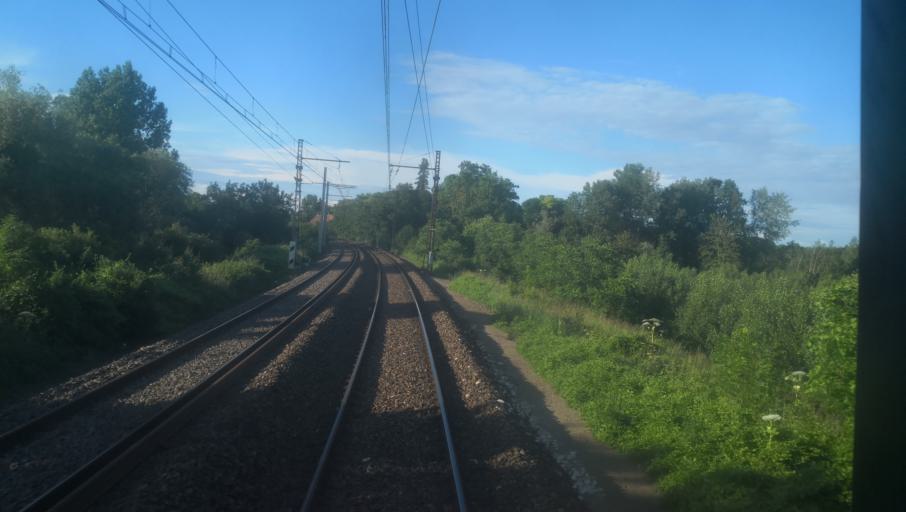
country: FR
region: Centre
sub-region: Departement de l'Indre
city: Sainte-Lizaigne
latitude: 47.0231
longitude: 2.0410
